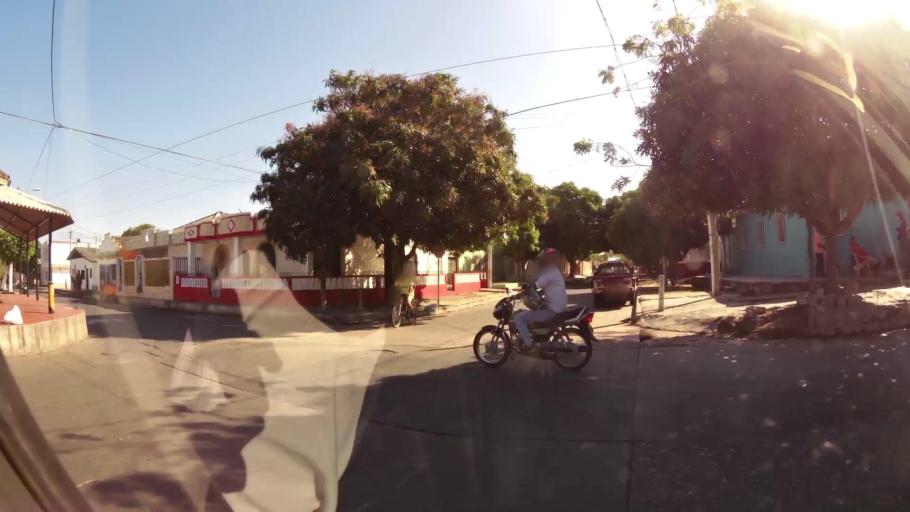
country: CO
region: Atlantico
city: Barranquilla
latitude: 10.9634
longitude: -74.7867
